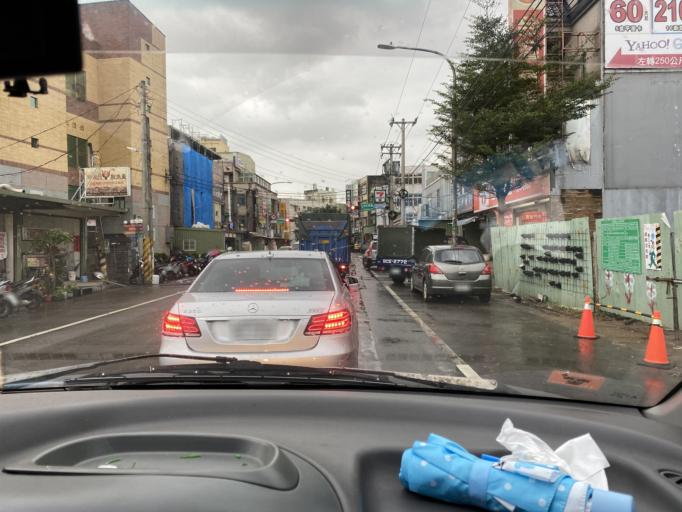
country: TW
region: Taiwan
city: Taoyuan City
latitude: 25.0623
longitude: 121.2004
